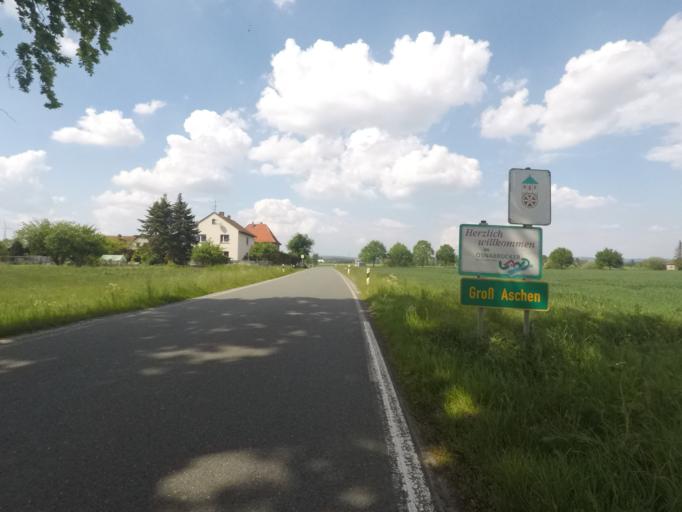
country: DE
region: North Rhine-Westphalia
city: Spenge
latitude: 52.1823
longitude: 8.5121
